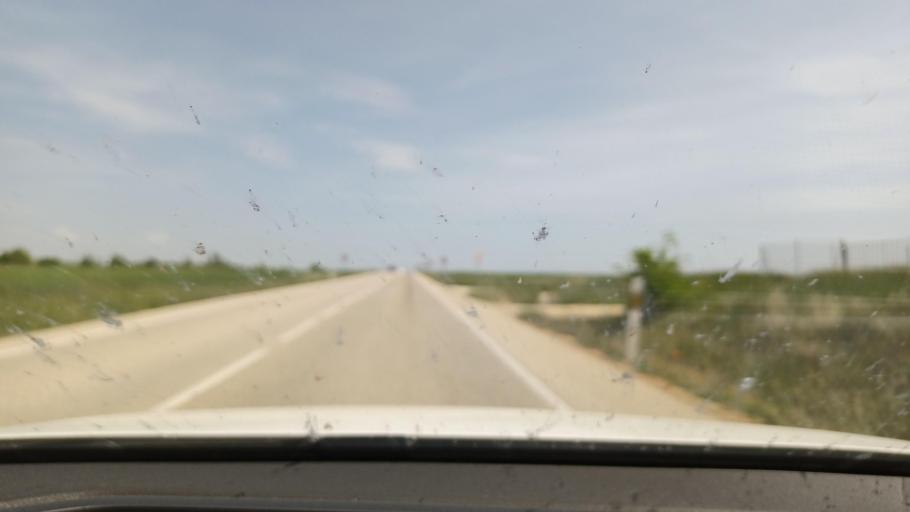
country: ES
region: Castille and Leon
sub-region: Provincia de Soria
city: Coscurita
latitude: 41.4599
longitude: -2.4942
